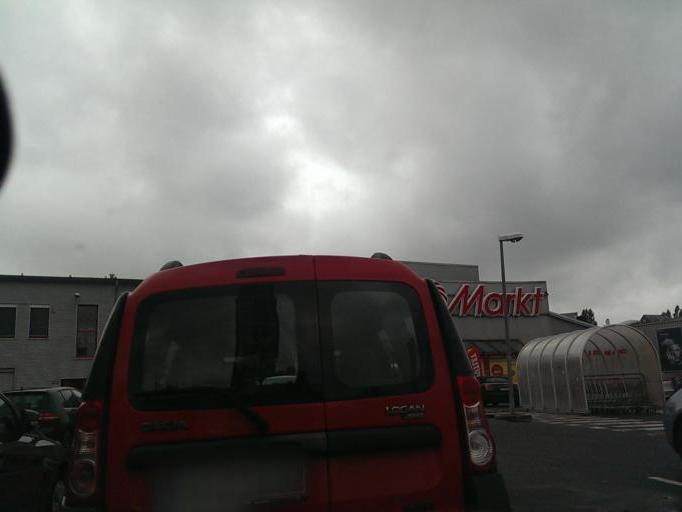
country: DE
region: Lower Saxony
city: Hannover
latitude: 52.4074
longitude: 9.7342
